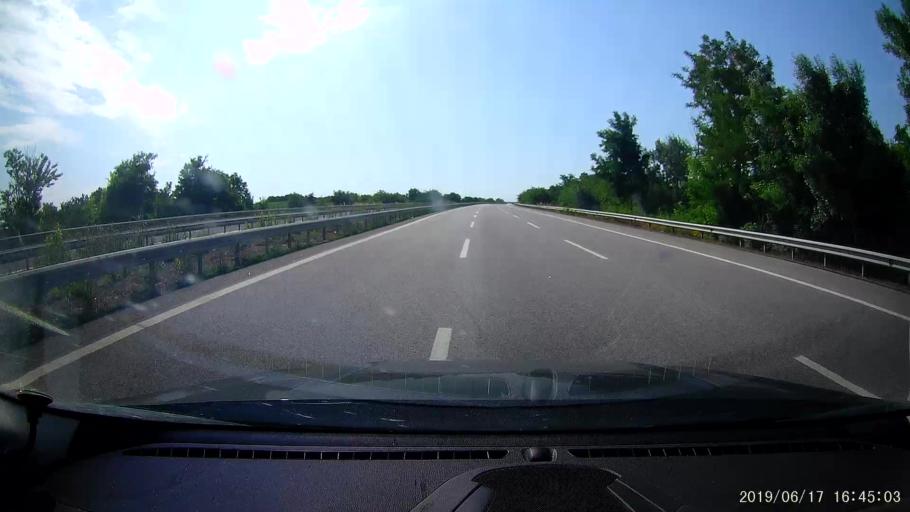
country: TR
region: Kirklareli
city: Luleburgaz
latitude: 41.4840
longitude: 27.2428
